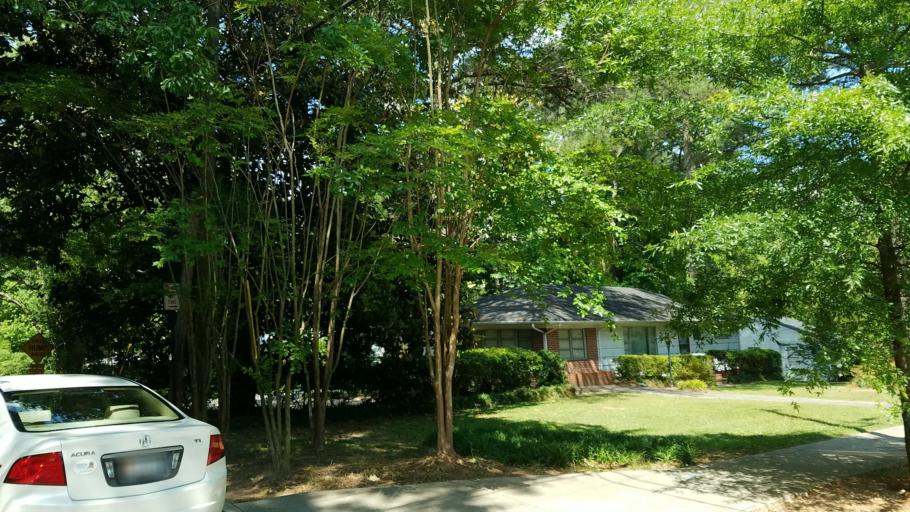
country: US
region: Georgia
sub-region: DeKalb County
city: Druid Hills
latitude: 33.8217
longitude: -84.3757
